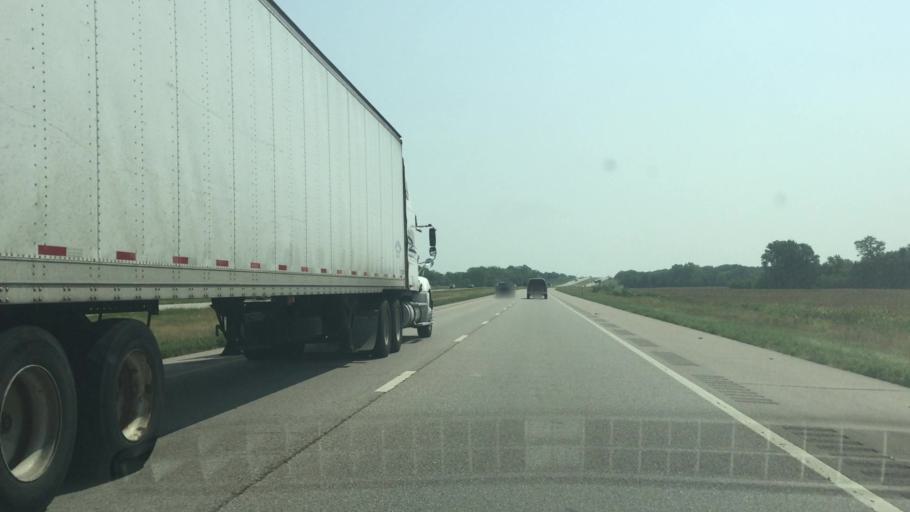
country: US
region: Kansas
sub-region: Lyon County
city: Emporia
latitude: 38.4111
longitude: -96.1155
